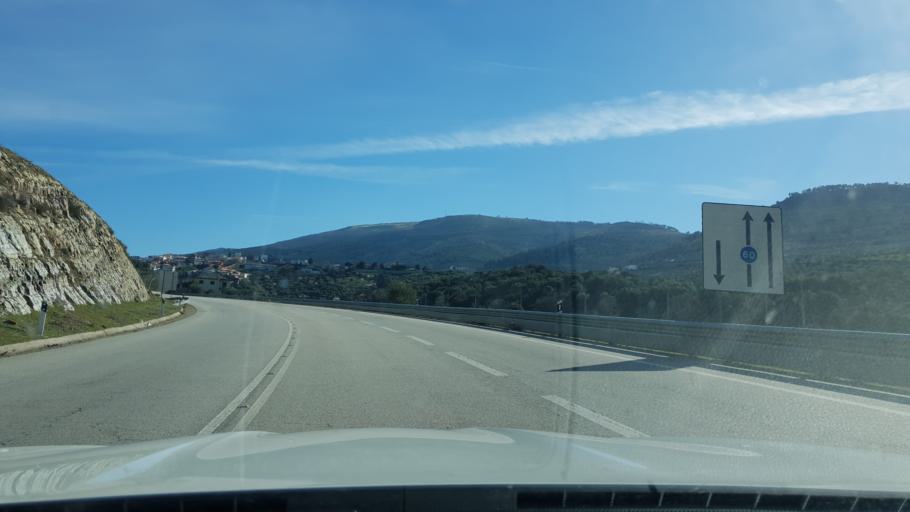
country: PT
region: Braganca
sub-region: Torre de Moncorvo
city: Torre de Moncorvo
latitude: 41.1774
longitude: -7.0715
